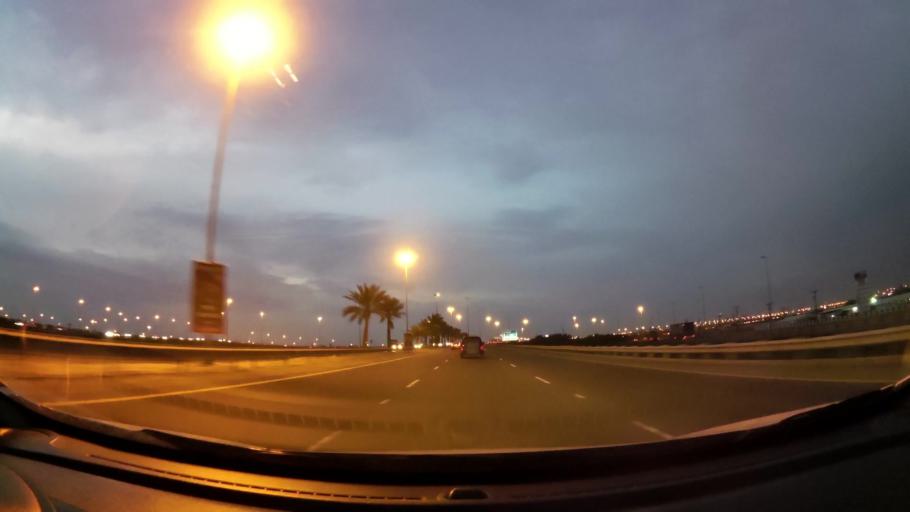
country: BH
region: Northern
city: Madinat `Isa
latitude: 26.1805
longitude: 50.5026
